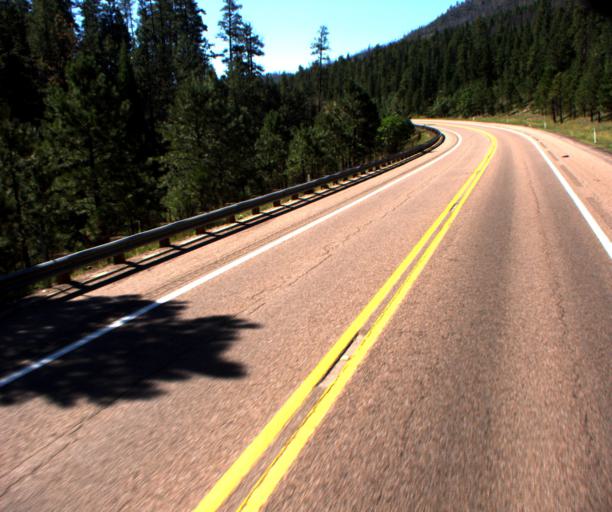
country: US
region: Arizona
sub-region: Apache County
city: Eagar
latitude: 33.9281
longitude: -109.1867
